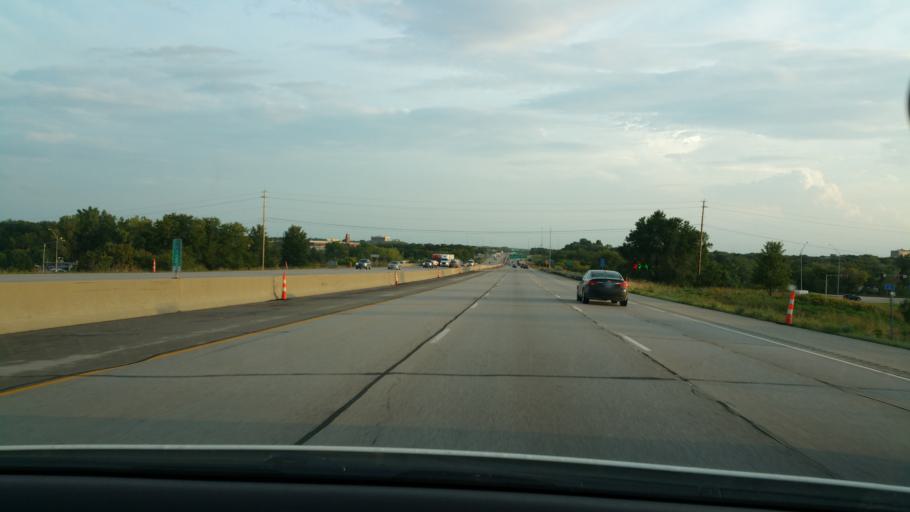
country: US
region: Iowa
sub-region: Polk County
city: Clive
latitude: 41.6170
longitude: -93.7771
